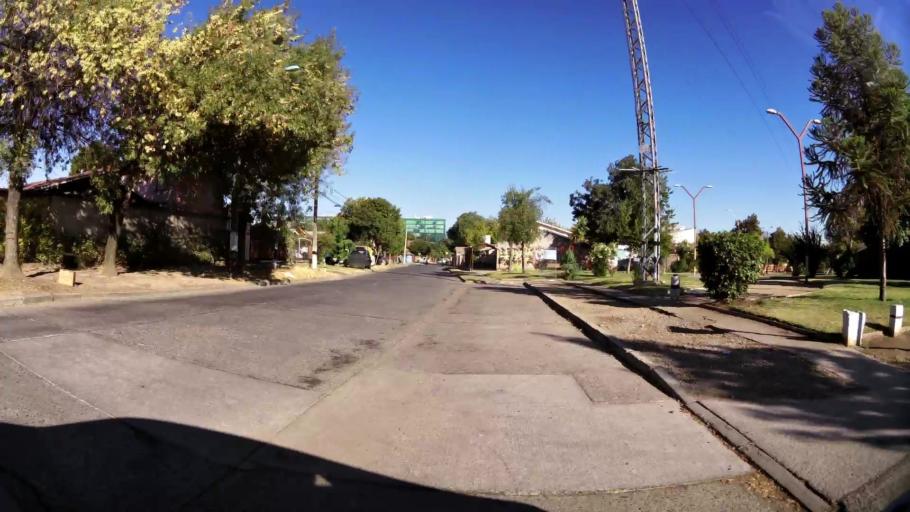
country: CL
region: O'Higgins
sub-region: Provincia de Cachapoal
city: Rancagua
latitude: -34.1811
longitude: -70.7257
